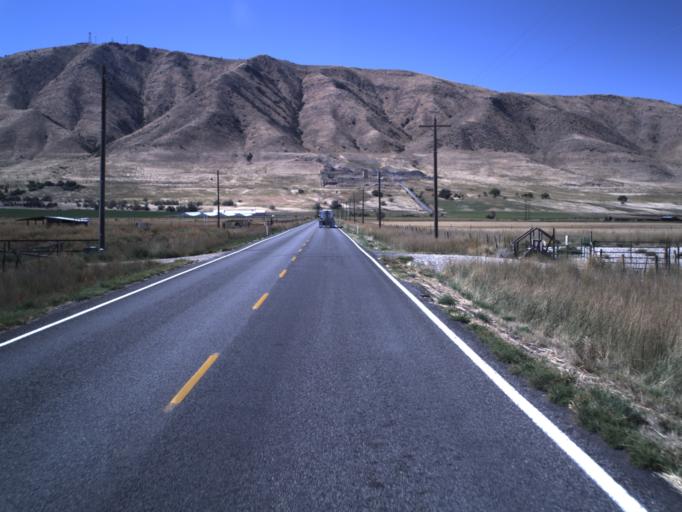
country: US
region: Utah
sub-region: Utah County
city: West Mountain
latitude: 40.0979
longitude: -111.7792
